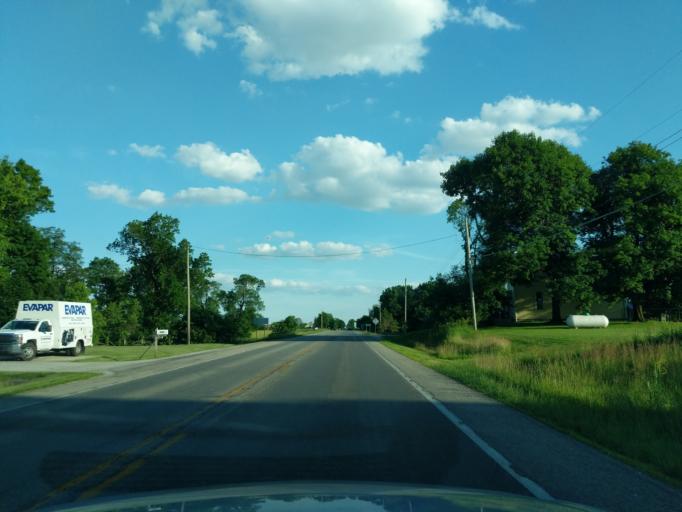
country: US
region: Indiana
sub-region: Huntington County
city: Huntington
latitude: 40.8631
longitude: -85.4709
